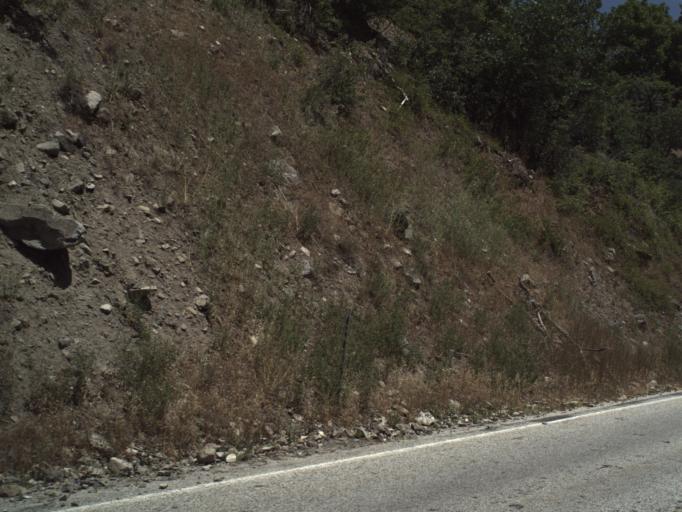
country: US
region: Utah
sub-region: Weber County
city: Liberty
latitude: 41.2550
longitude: -111.8633
